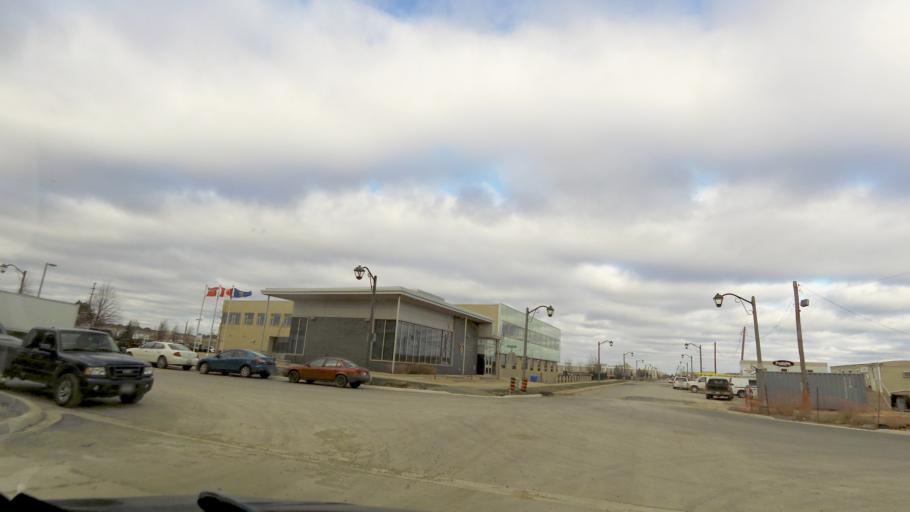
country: CA
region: Ontario
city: Oakville
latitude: 43.4802
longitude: -79.7260
